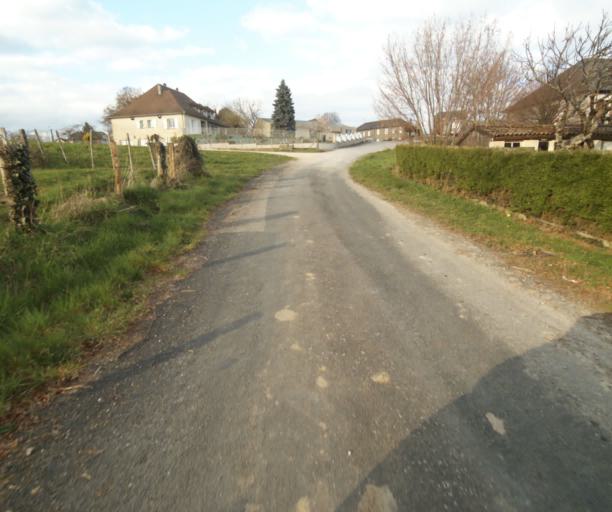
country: FR
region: Limousin
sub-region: Departement de la Correze
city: Saint-Clement
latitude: 45.3558
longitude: 1.6380
